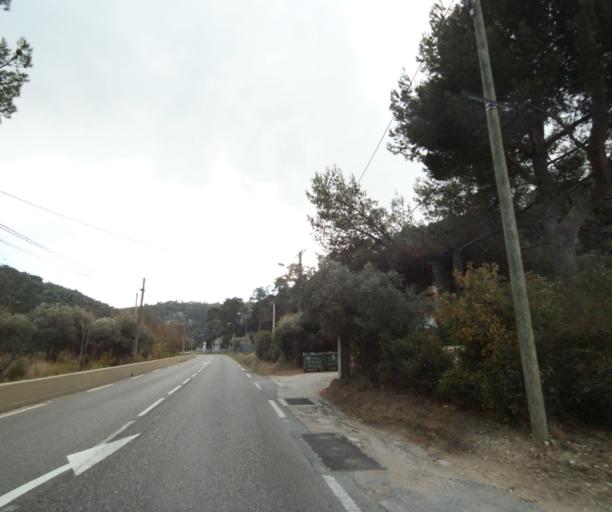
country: FR
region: Provence-Alpes-Cote d'Azur
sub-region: Departement des Bouches-du-Rhone
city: Gemenos
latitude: 43.2707
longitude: 5.6454
